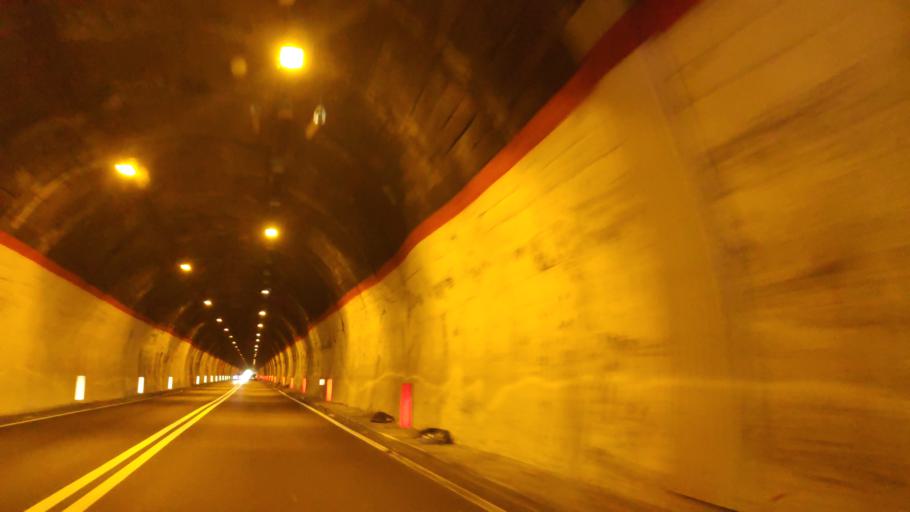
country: IT
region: Calabria
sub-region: Provincia di Cosenza
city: Praia a Mare
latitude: 39.9015
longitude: 15.7907
